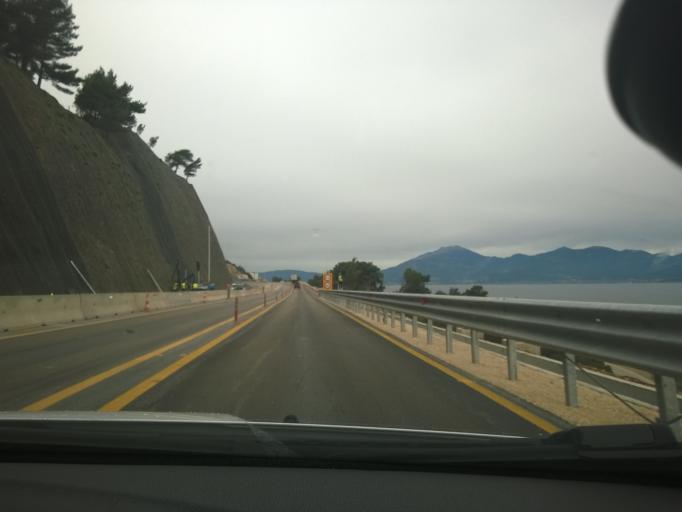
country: GR
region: West Greece
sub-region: Nomos Achaias
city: Kamarai
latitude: 38.3242
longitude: 21.9620
